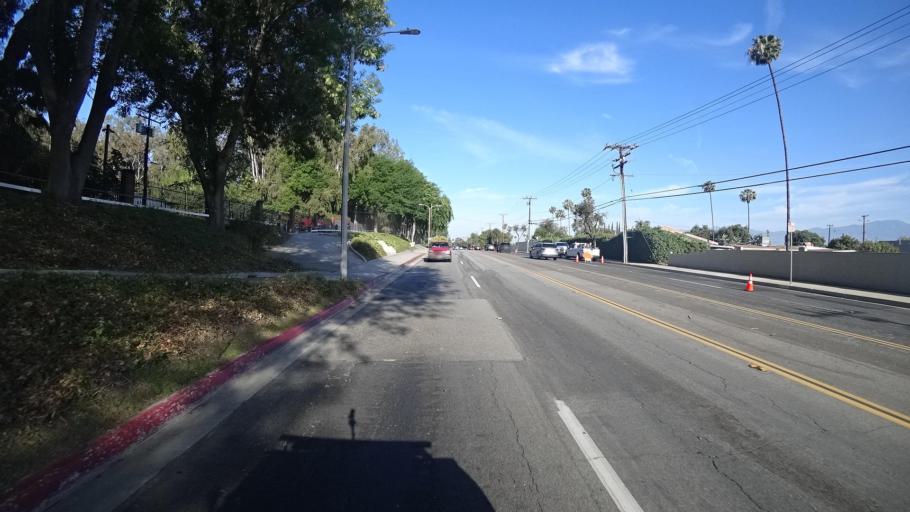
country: US
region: California
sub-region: Los Angeles County
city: South San Jose Hills
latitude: 34.0257
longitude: -117.9248
